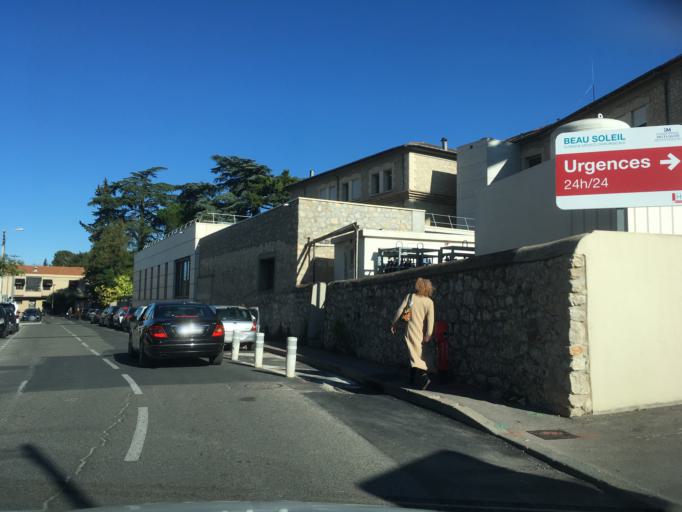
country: FR
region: Languedoc-Roussillon
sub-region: Departement de l'Herault
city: Montpellier
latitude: 43.6096
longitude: 3.8491
